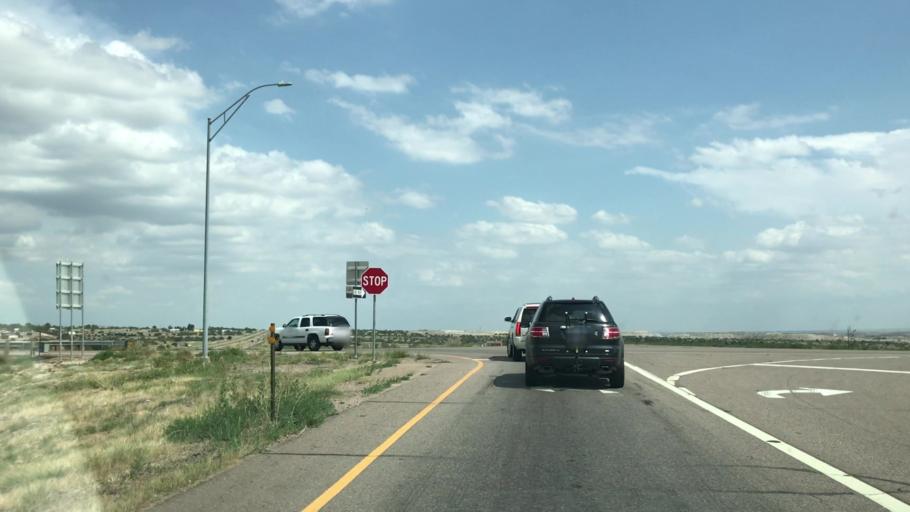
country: US
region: Colorado
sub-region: Fremont County
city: Penrose
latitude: 38.4182
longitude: -105.0430
